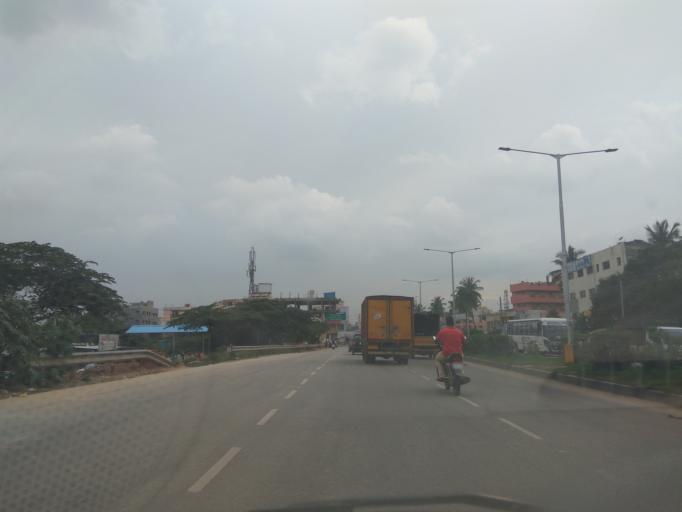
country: IN
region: Karnataka
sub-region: Bangalore Urban
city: Bangalore
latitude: 13.0114
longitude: 77.6986
